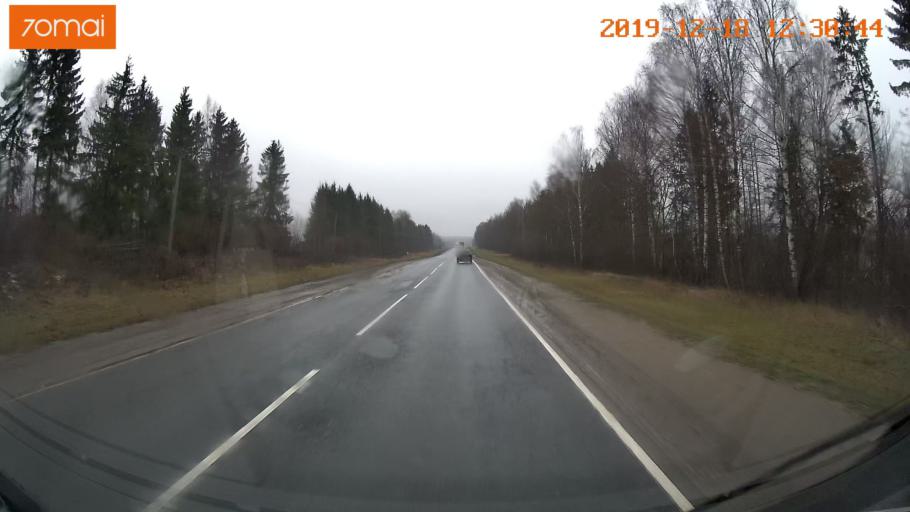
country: RU
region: Moskovskaya
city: Novopetrovskoye
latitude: 56.0926
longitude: 36.5358
